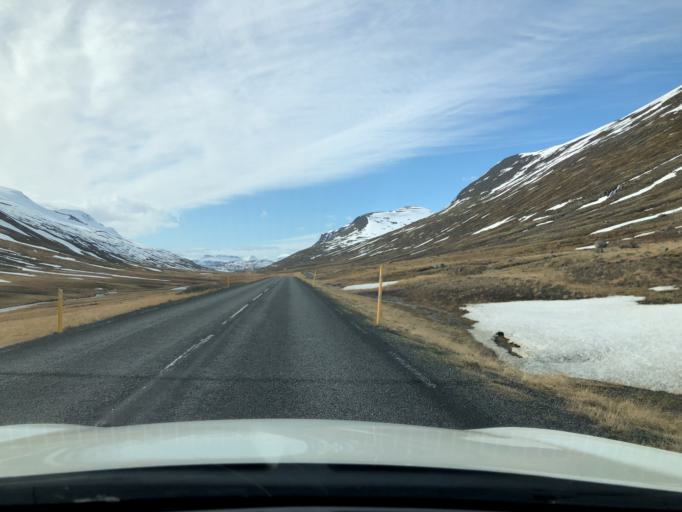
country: IS
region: East
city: Egilsstadir
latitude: 65.1505
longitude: -14.3396
